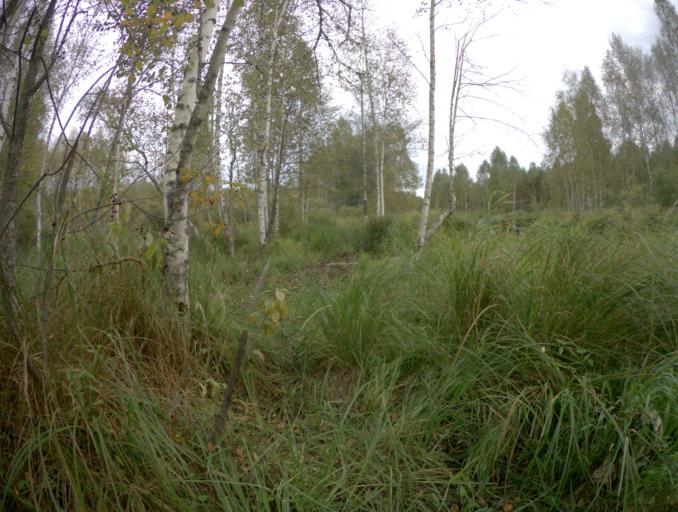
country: RU
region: Vladimir
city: Urshel'skiy
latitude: 55.8211
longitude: 40.2742
